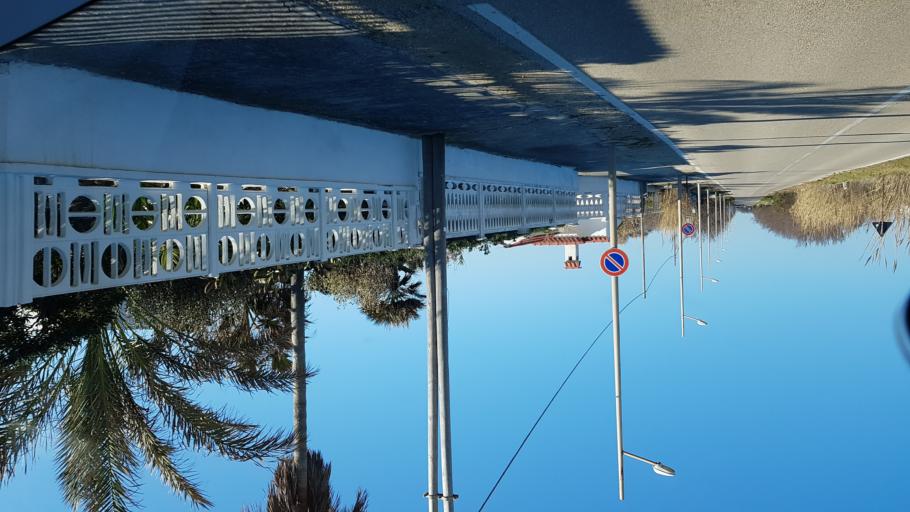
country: IT
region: Apulia
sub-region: Provincia di Brindisi
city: Brindisi
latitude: 40.6927
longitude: 17.8340
